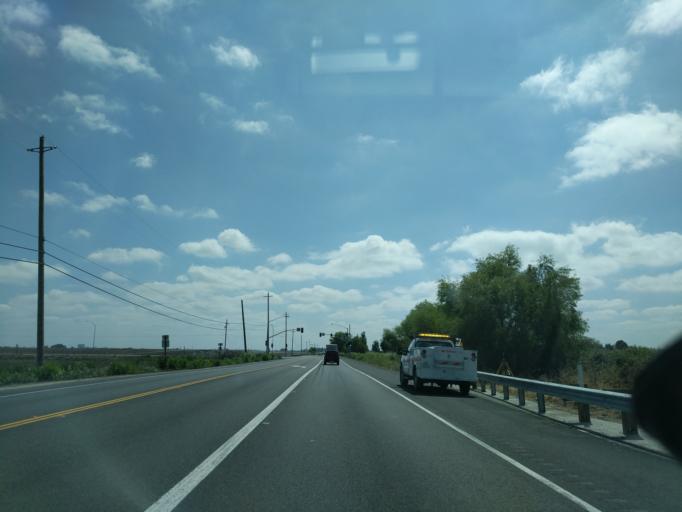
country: US
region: California
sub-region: San Joaquin County
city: Country Club
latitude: 37.9269
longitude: -121.3629
